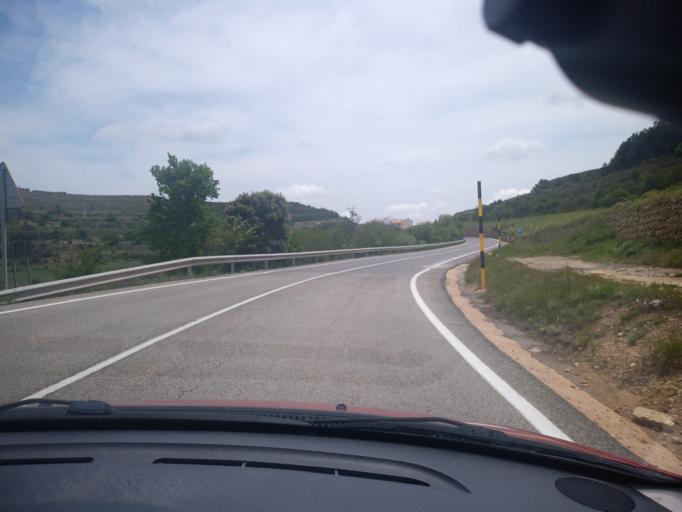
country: ES
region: Valencia
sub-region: Provincia de Castello
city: Ares del Maestre
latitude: 40.4578
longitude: -0.1475
